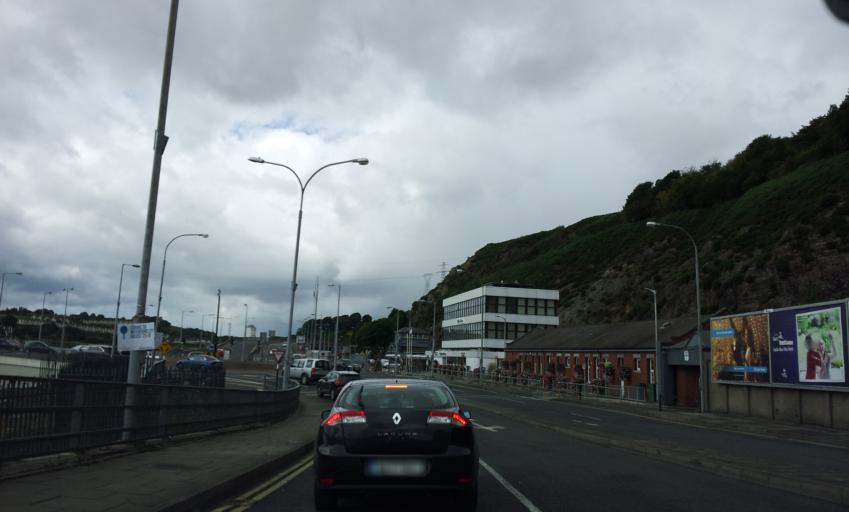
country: IE
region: Munster
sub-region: Waterford
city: Waterford
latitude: 52.2657
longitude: -7.1166
